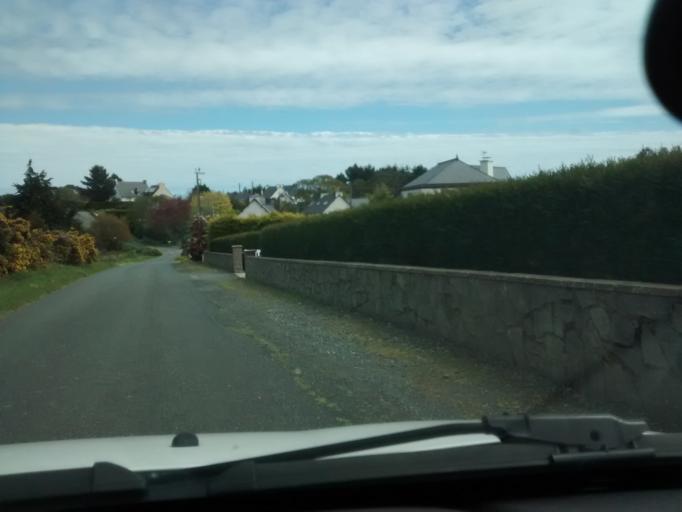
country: FR
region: Brittany
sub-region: Departement des Cotes-d'Armor
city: Ploubazlanec
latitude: 48.8028
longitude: -3.0118
